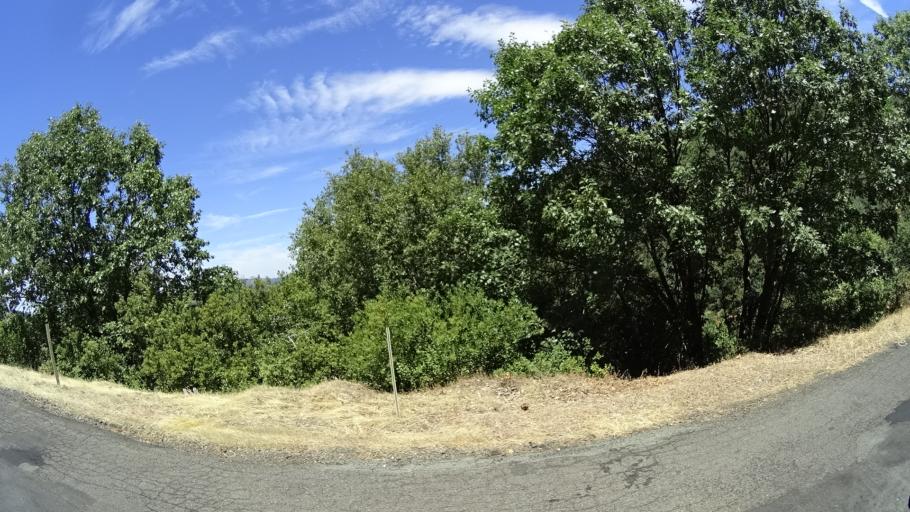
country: US
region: California
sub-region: Calaveras County
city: Forest Meadows
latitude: 38.1943
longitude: -120.4412
